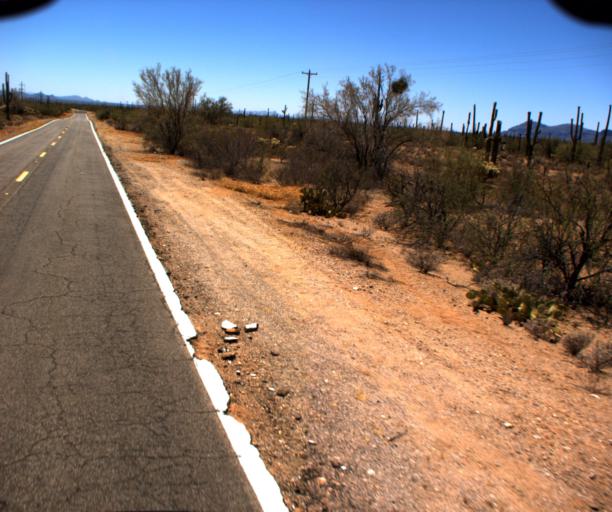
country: US
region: Arizona
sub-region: Pima County
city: Sells
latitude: 32.1472
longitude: -112.1026
